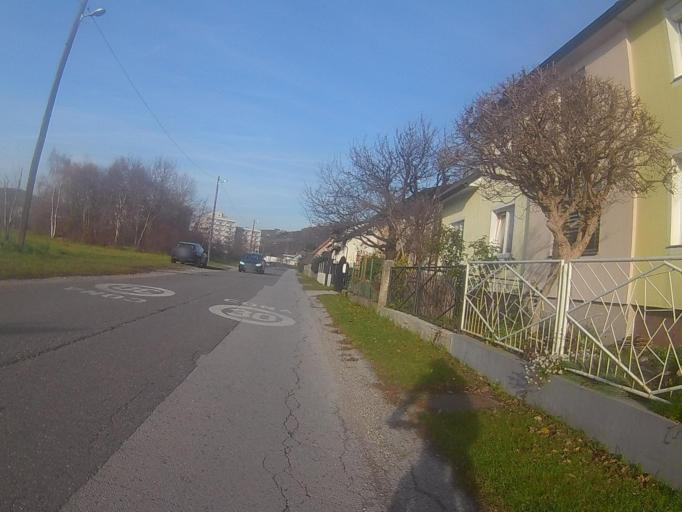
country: SI
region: Maribor
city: Maribor
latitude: 46.5519
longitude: 15.6687
